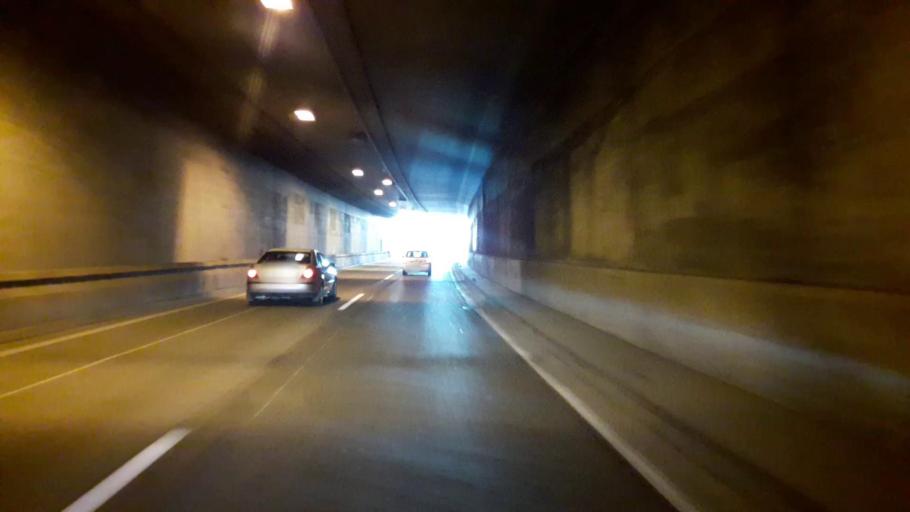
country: AT
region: Lower Austria
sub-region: Politischer Bezirk Wien-Umgebung
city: Gerasdorf bei Wien
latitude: 48.2334
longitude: 16.4545
